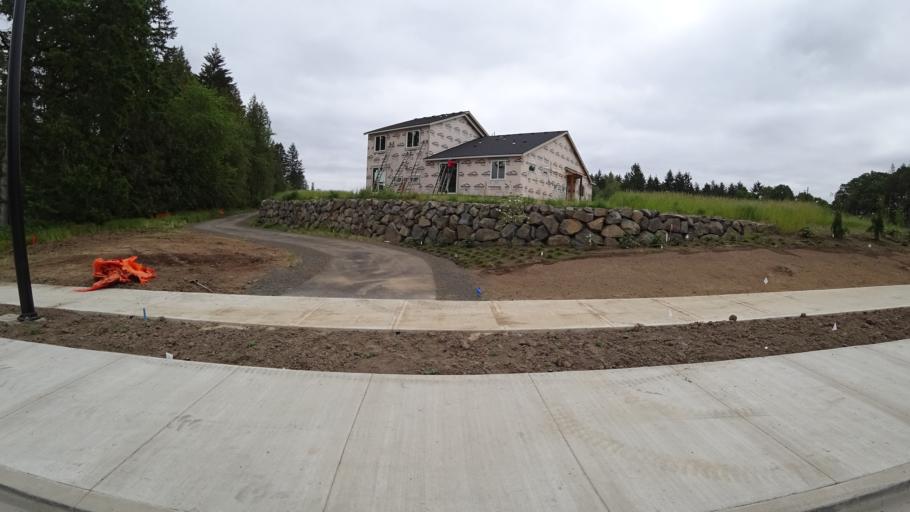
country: US
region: Oregon
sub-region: Washington County
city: Aloha
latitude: 45.4933
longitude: -122.9192
